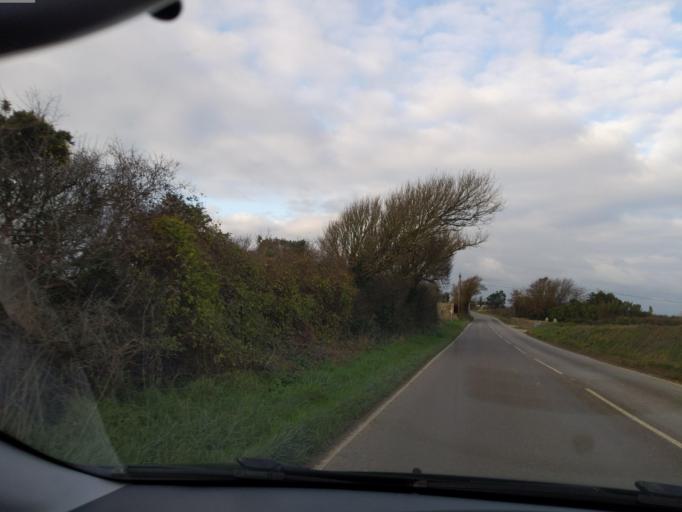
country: GB
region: England
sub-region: Cornwall
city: Padstow
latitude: 50.5213
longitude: -4.9517
